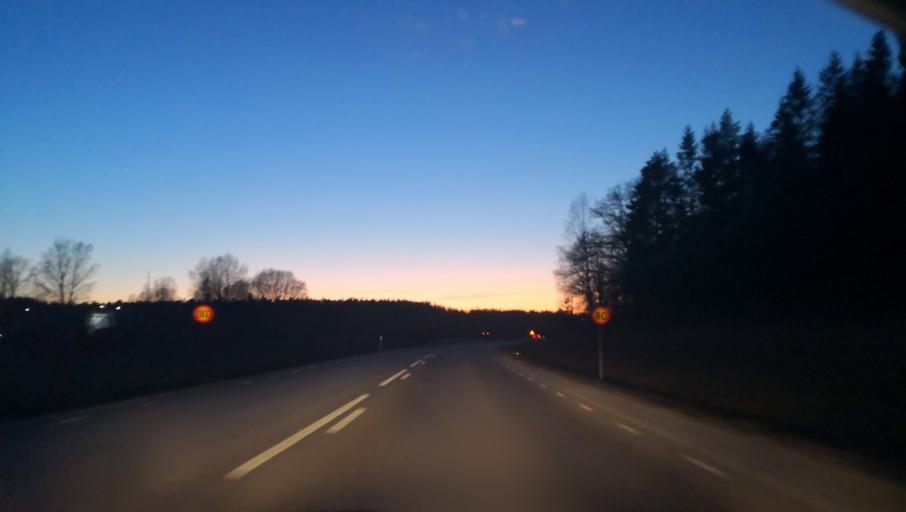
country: SE
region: Stockholm
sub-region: Nynashamns Kommun
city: Nynashamn
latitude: 58.9298
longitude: 17.9307
